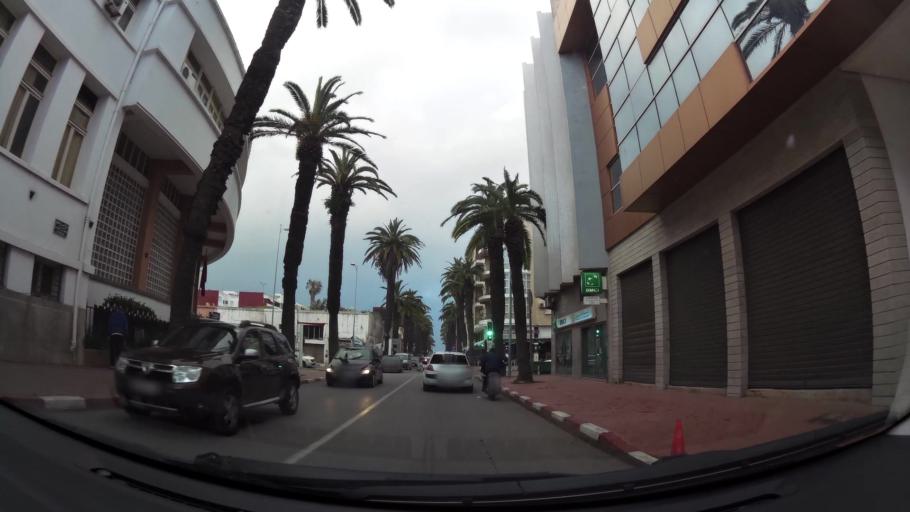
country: MA
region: Doukkala-Abda
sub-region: El-Jadida
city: El Jadida
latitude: 33.2482
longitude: -8.5014
